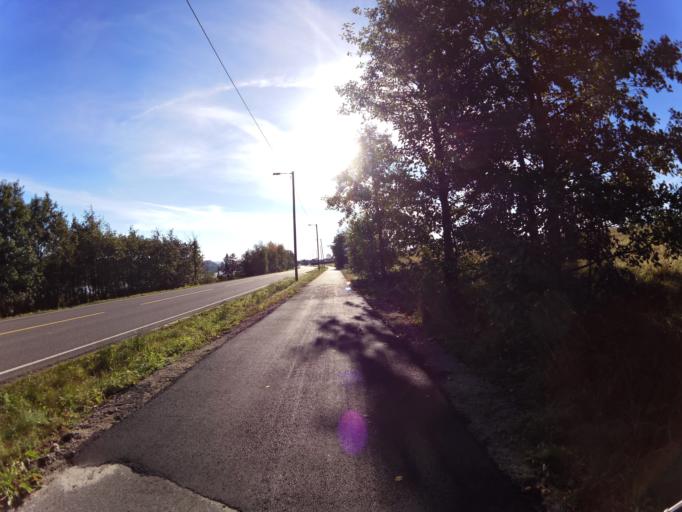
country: NO
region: Ostfold
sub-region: Fredrikstad
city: Fredrikstad
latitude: 59.2870
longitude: 11.0057
